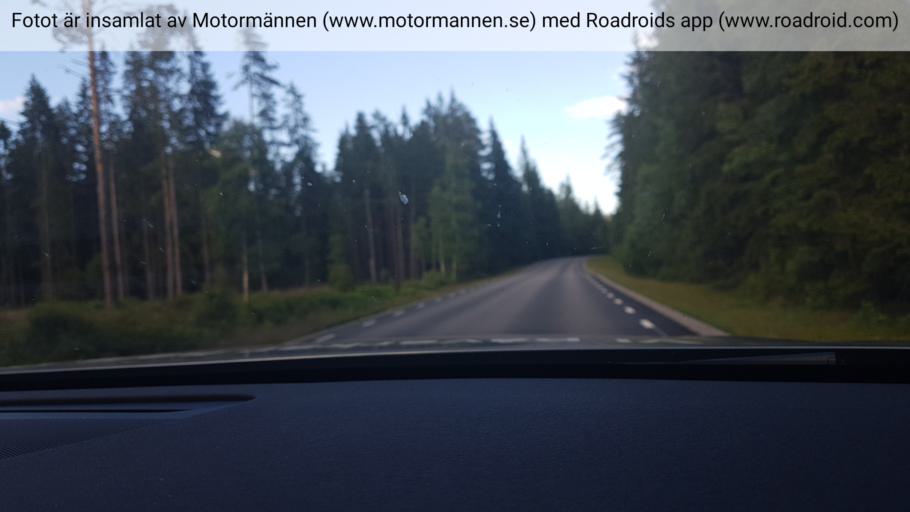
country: SE
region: Joenkoeping
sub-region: Gnosjo Kommun
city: Gnosjoe
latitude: 57.5733
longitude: 13.6329
